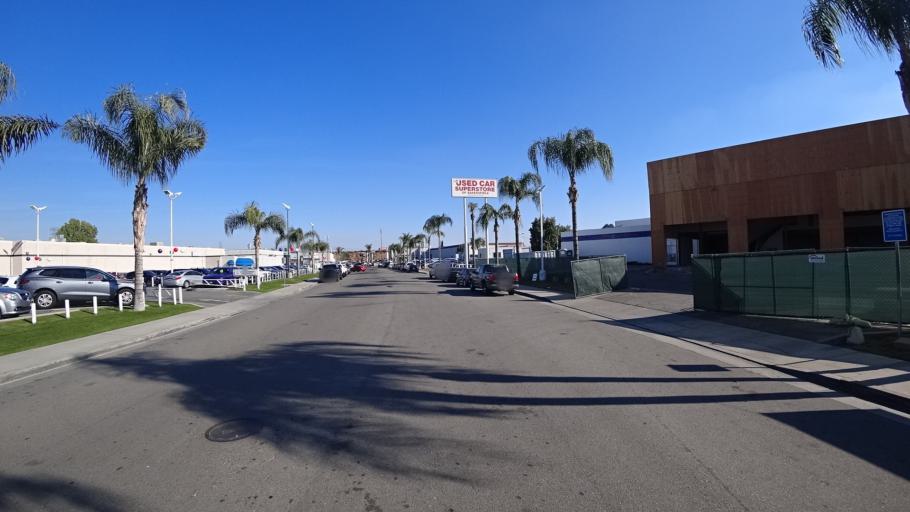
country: US
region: California
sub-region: Kern County
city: Greenfield
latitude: 35.3116
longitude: -119.0385
